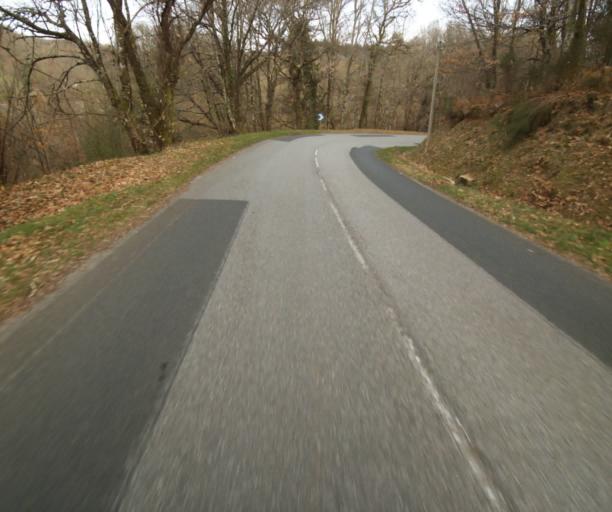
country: FR
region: Limousin
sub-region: Departement de la Correze
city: Treignac
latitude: 45.4455
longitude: 1.8055
